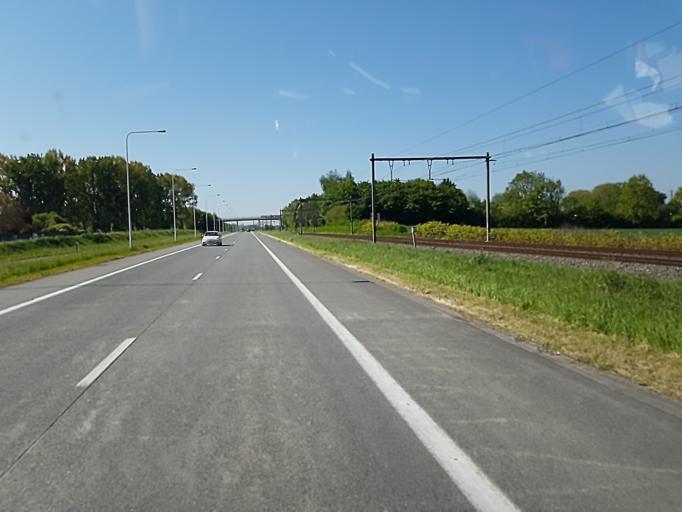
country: BE
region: Wallonia
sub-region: Province du Hainaut
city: Ath
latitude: 50.6560
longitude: 3.7901
